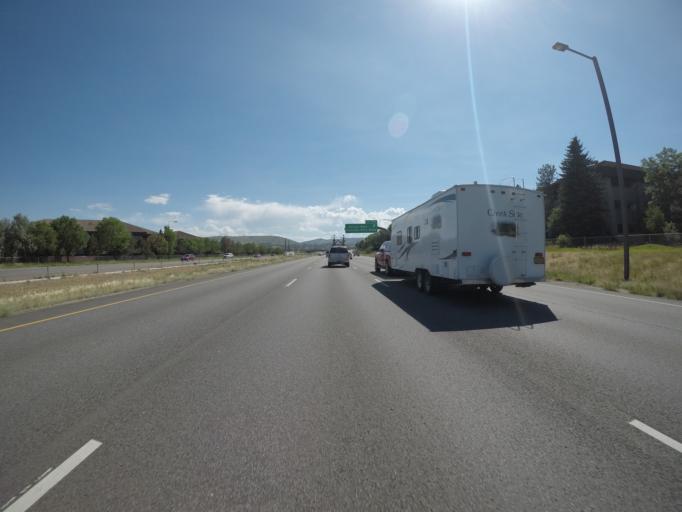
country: US
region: Colorado
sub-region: Jefferson County
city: Applewood
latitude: 39.7442
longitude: -105.1541
